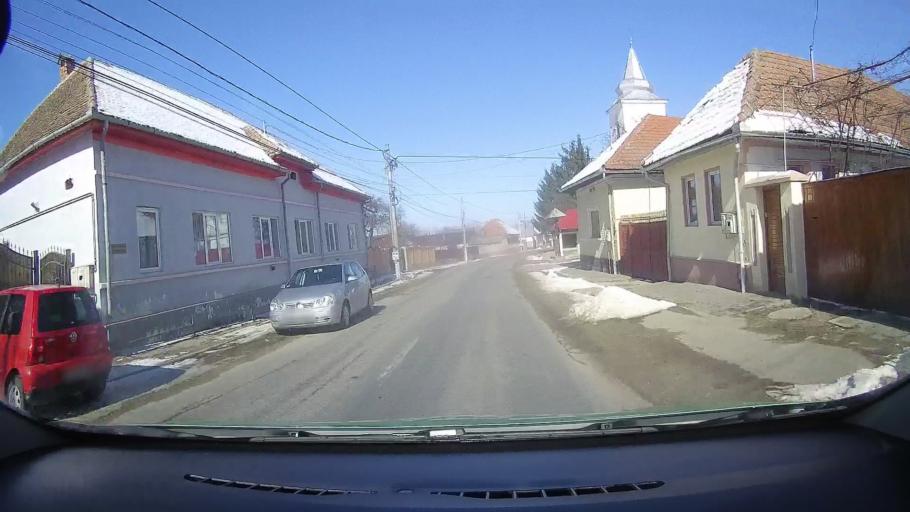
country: RO
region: Brasov
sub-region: Oras Victoria
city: Victoria
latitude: 45.7462
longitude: 24.7397
